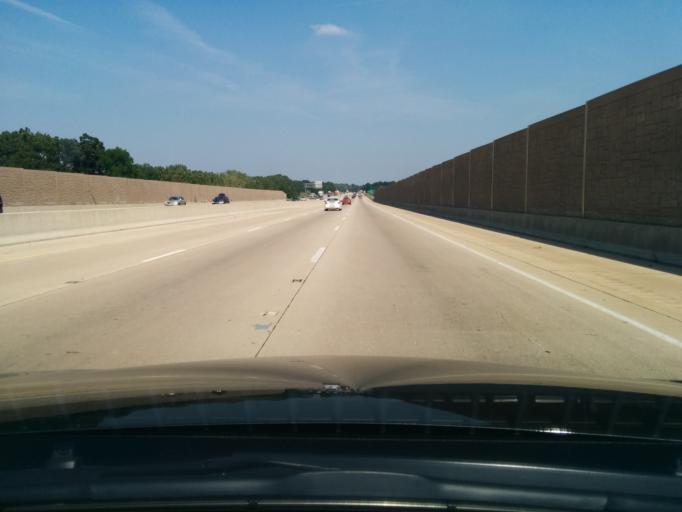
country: US
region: Illinois
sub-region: Will County
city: New Lenox
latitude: 41.5433
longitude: -87.9386
